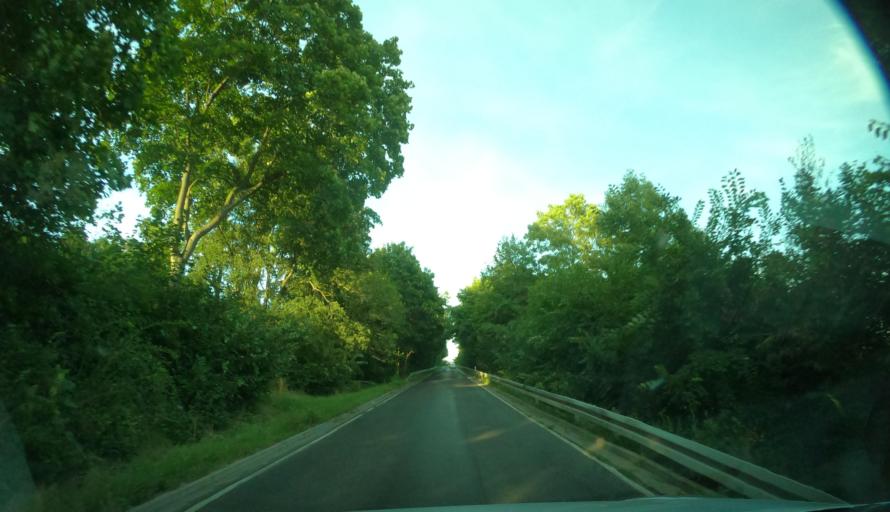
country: PL
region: Kujawsko-Pomorskie
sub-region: Powiat swiecki
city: Pruszcz
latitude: 53.2348
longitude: 18.2160
